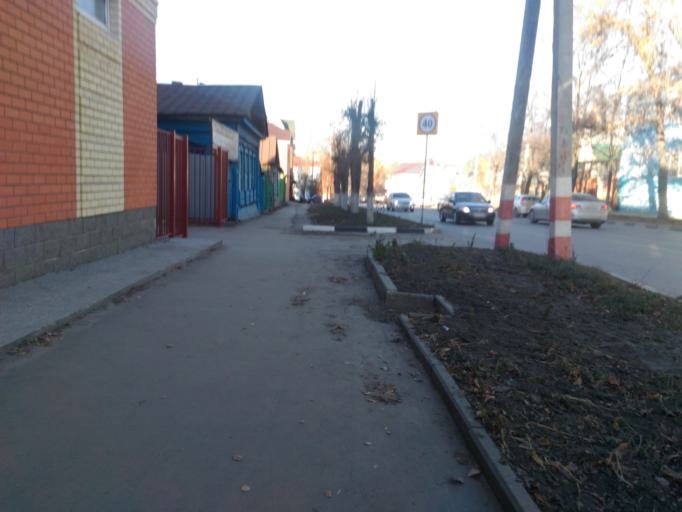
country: RU
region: Ulyanovsk
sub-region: Ulyanovskiy Rayon
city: Ulyanovsk
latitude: 54.3113
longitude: 48.3785
